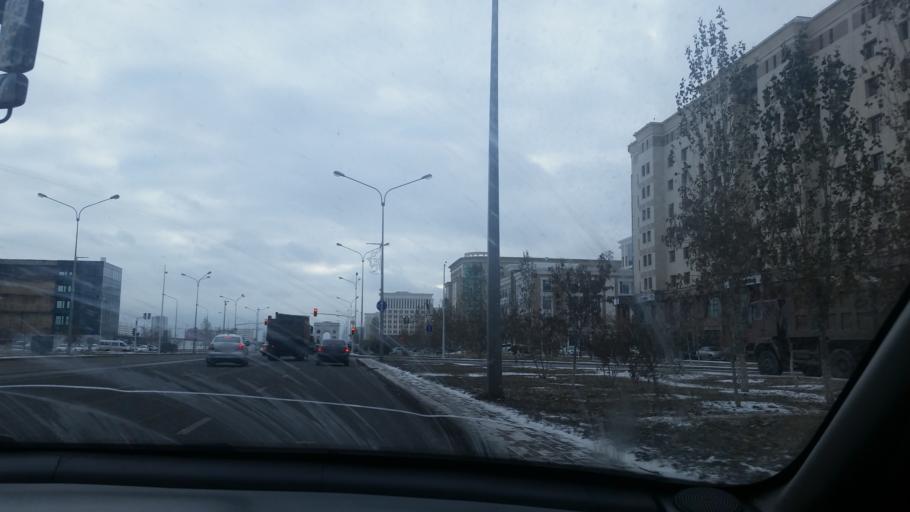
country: KZ
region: Astana Qalasy
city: Astana
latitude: 51.1100
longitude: 71.4320
